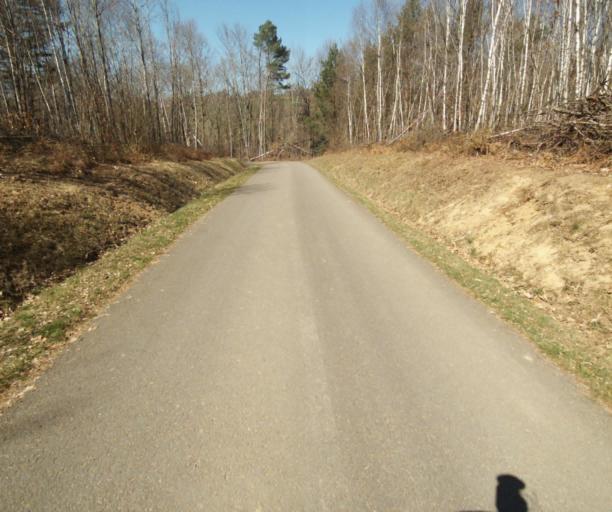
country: FR
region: Limousin
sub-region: Departement de la Correze
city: Chameyrat
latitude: 45.2815
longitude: 1.7050
